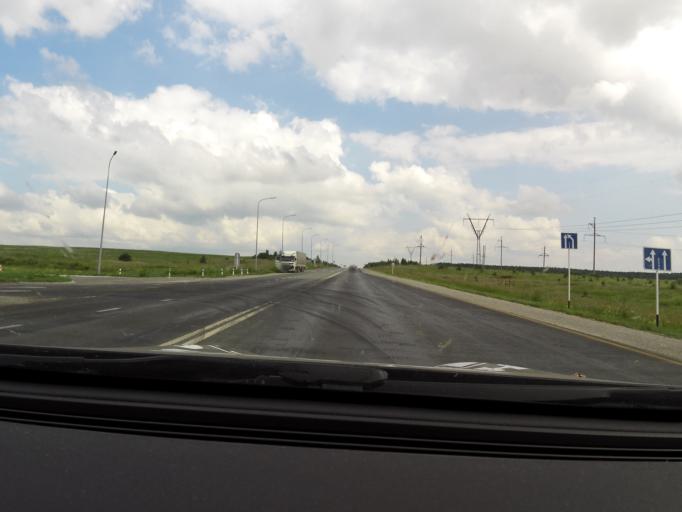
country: RU
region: Sverdlovsk
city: Achit
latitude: 56.7823
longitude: 57.9095
